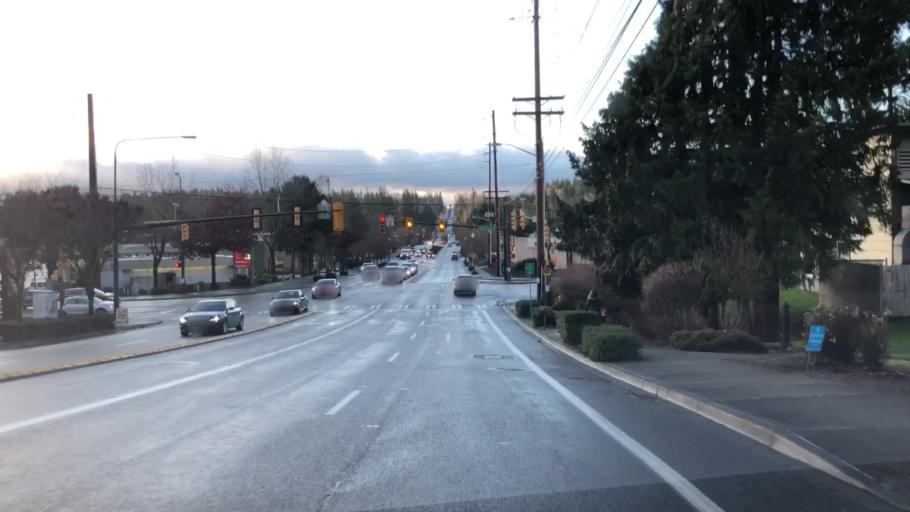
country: US
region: Washington
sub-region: King County
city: City of Sammamish
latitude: 47.6172
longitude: -122.0356
